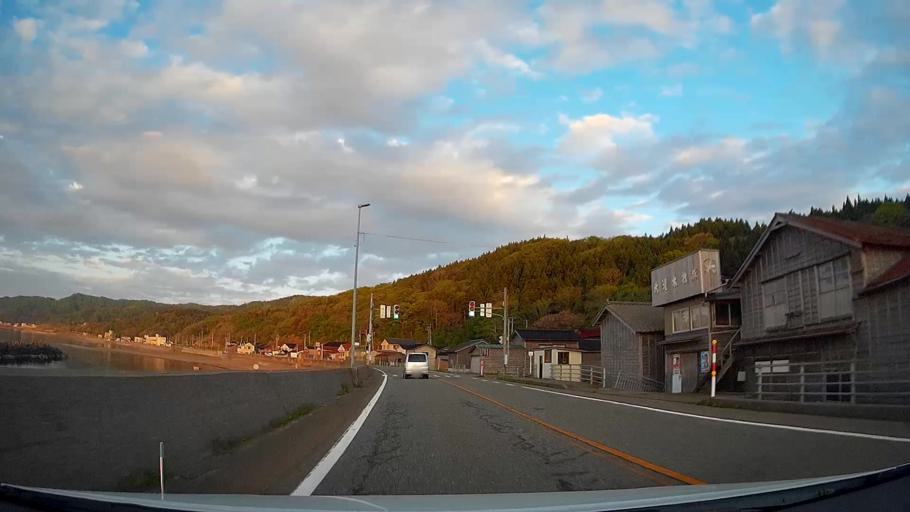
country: JP
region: Niigata
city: Itoigawa
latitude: 37.1144
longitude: 138.0168
